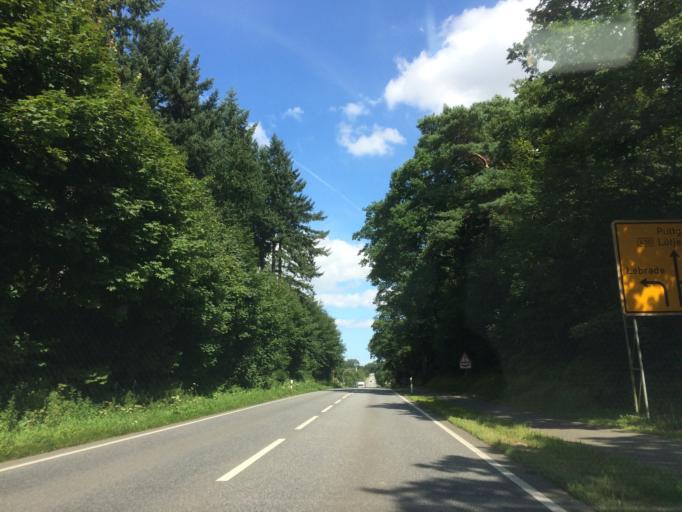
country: DE
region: Schleswig-Holstein
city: Grebin
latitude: 54.1998
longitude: 10.4716
